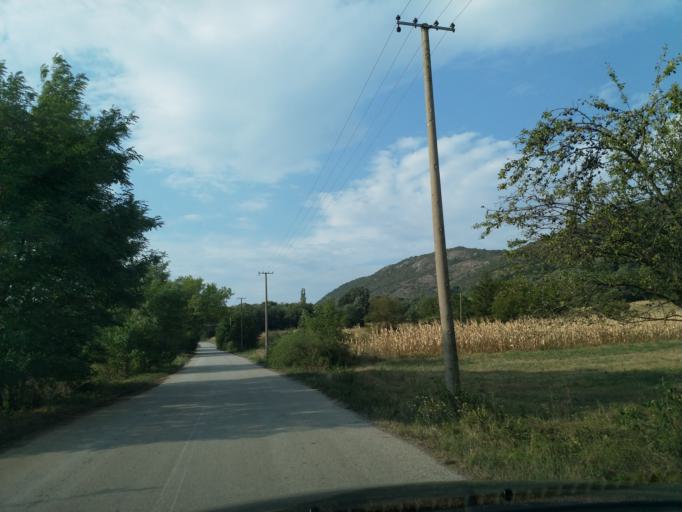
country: RS
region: Central Serbia
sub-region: Pomoravski Okrug
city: Paracin
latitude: 43.8312
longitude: 21.5420
